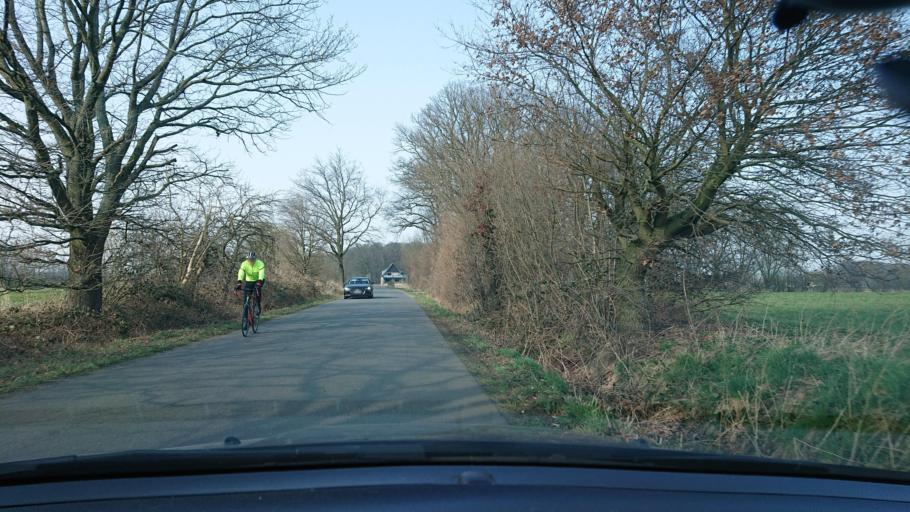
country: DE
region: North Rhine-Westphalia
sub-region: Regierungsbezirk Detmold
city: Langenberg
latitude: 51.7575
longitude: 8.3737
